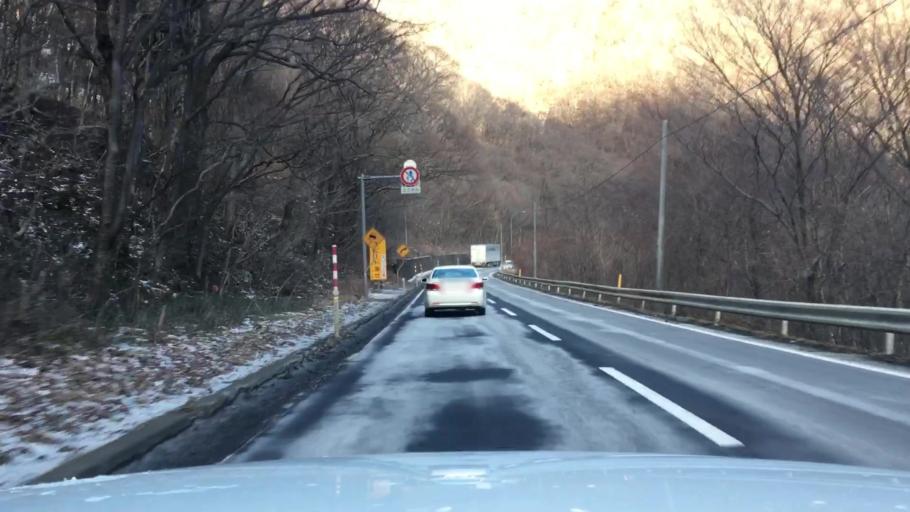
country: JP
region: Iwate
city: Tono
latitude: 39.6193
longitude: 141.5047
